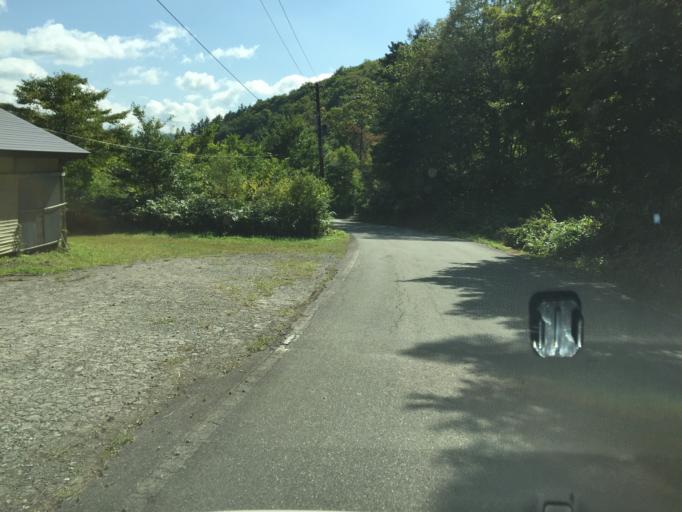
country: JP
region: Fukushima
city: Inawashiro
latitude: 37.6446
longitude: 140.2208
